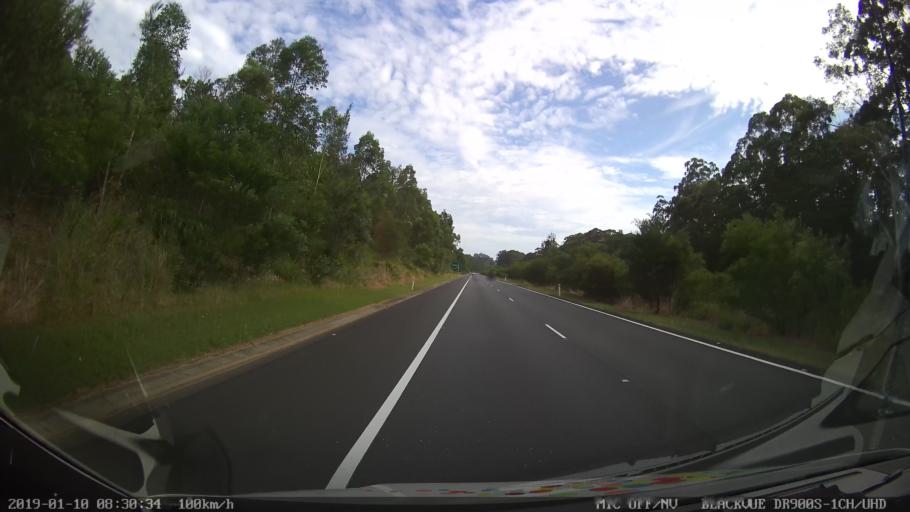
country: AU
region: New South Wales
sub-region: Coffs Harbour
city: Bonville
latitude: -30.3680
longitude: 153.0543
